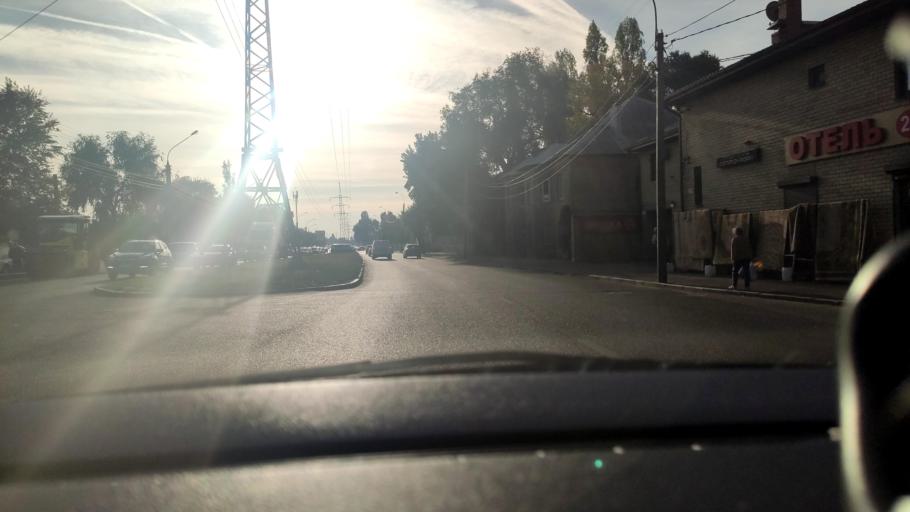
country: RU
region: Voronezj
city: Voronezh
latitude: 51.6395
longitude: 39.1619
